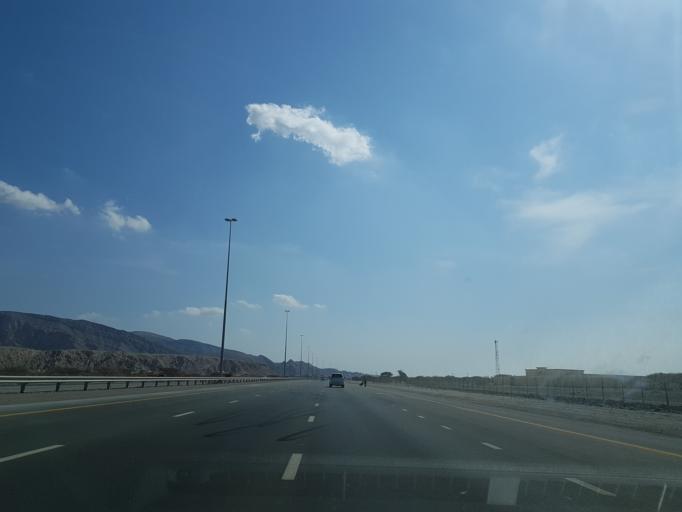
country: AE
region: Ra's al Khaymah
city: Ras al-Khaimah
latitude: 25.7931
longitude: 56.0309
